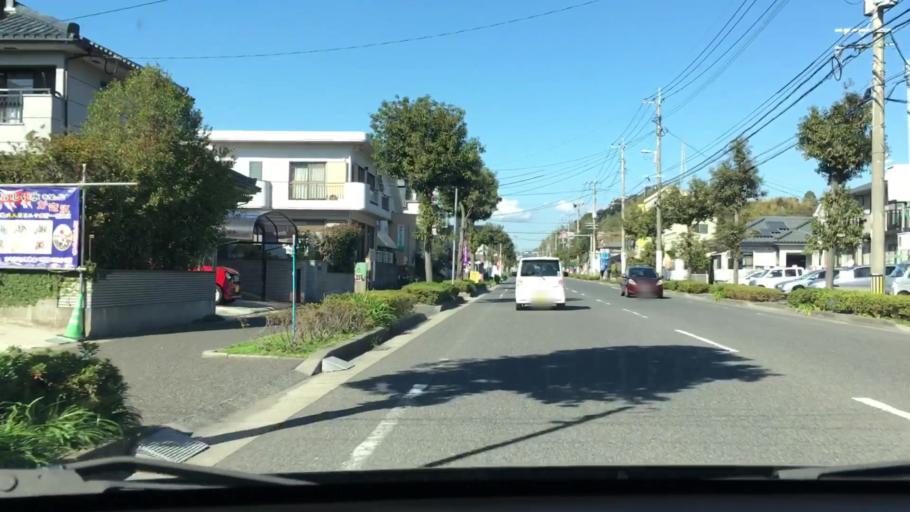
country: JP
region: Kagoshima
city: Kagoshima-shi
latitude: 31.5493
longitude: 130.5319
